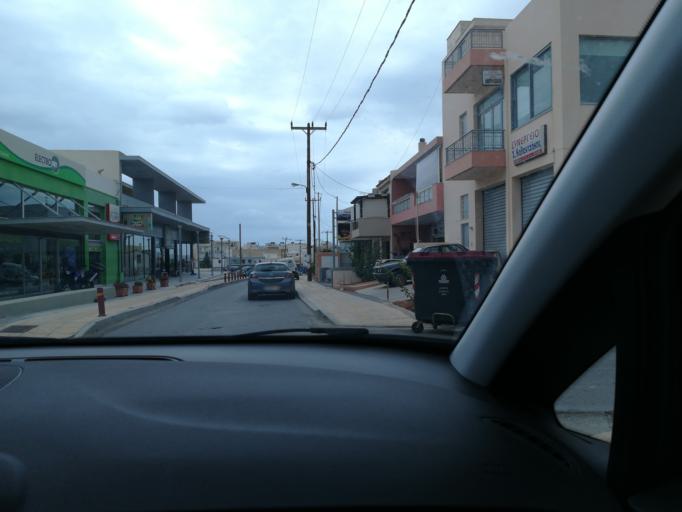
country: GR
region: Crete
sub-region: Nomos Lasithiou
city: Siteia
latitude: 35.2043
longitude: 26.1015
